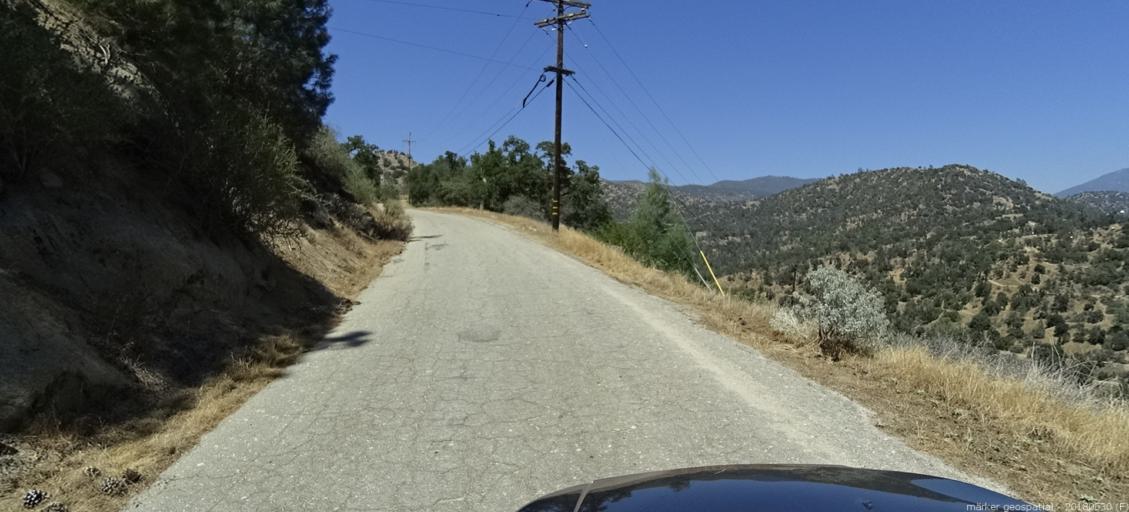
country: US
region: California
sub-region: Fresno County
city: Auberry
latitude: 37.1466
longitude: -119.4639
